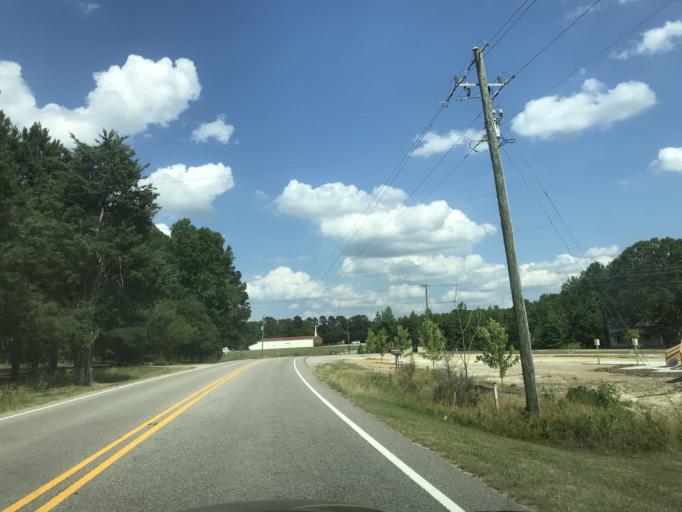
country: US
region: North Carolina
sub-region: Wake County
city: Rolesville
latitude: 35.9765
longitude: -78.3518
